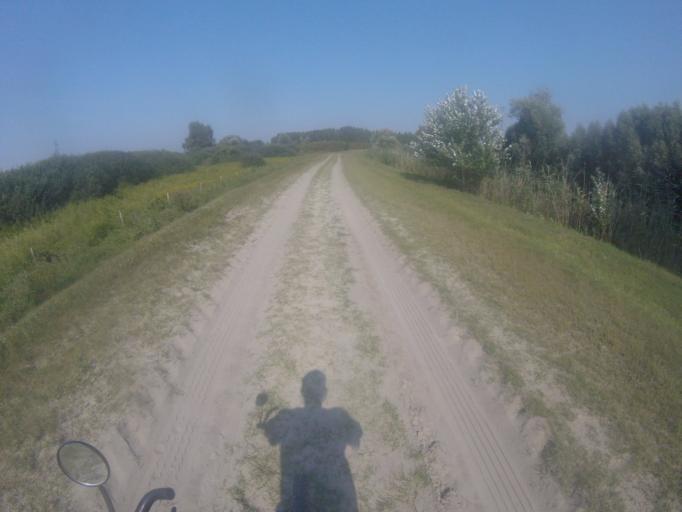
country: HU
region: Bacs-Kiskun
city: Baja
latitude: 46.2148
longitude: 18.9559
